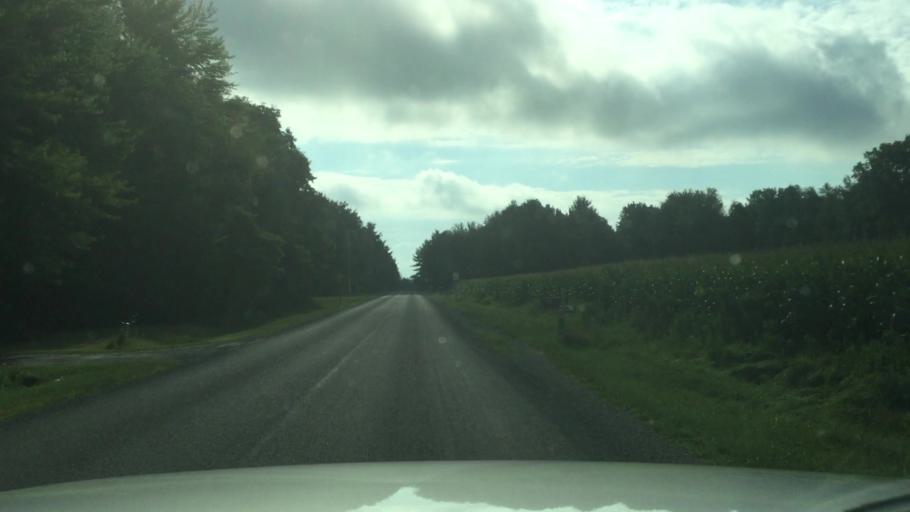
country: US
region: Michigan
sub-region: Saginaw County
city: Frankenmuth
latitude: 43.2788
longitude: -83.7135
